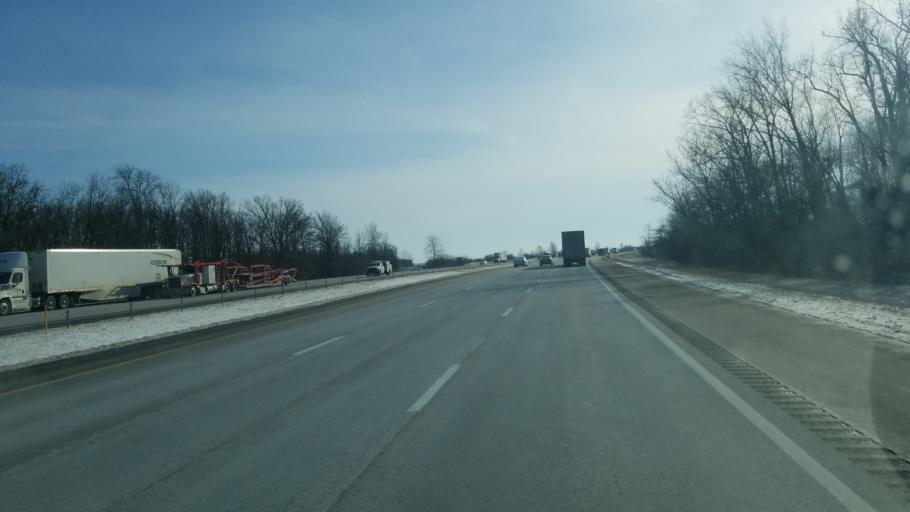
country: US
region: Ohio
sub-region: Wood County
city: Bowling Green
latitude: 41.3099
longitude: -83.6272
